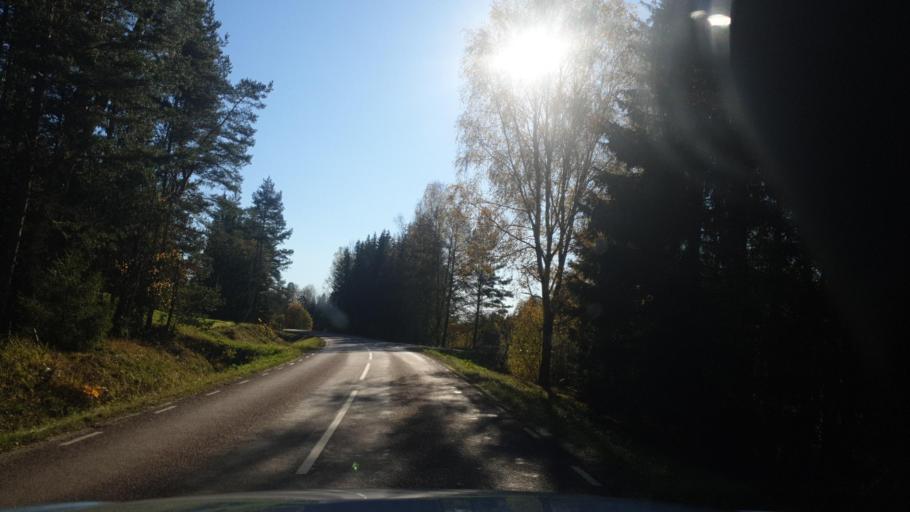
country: SE
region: Vaermland
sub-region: Grums Kommun
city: Slottsbron
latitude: 59.4217
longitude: 12.9814
